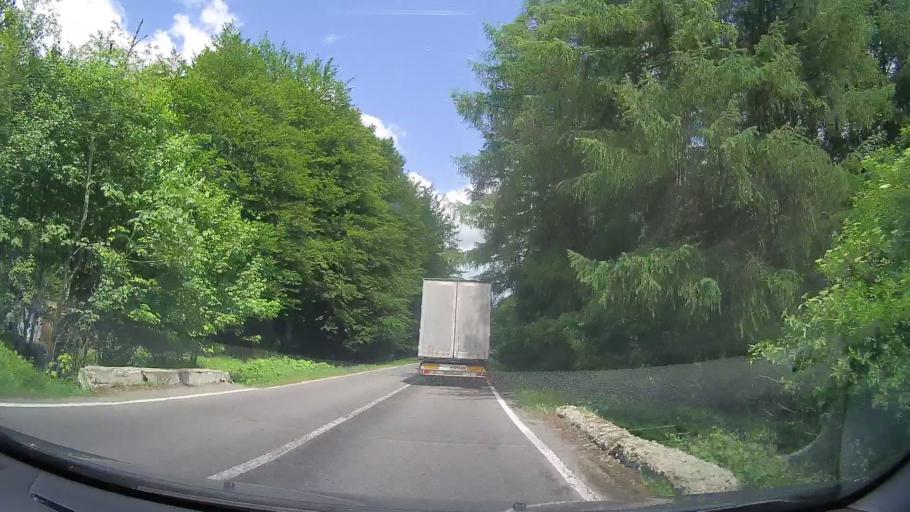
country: RO
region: Prahova
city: Maneciu
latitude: 45.4123
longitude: 25.9426
